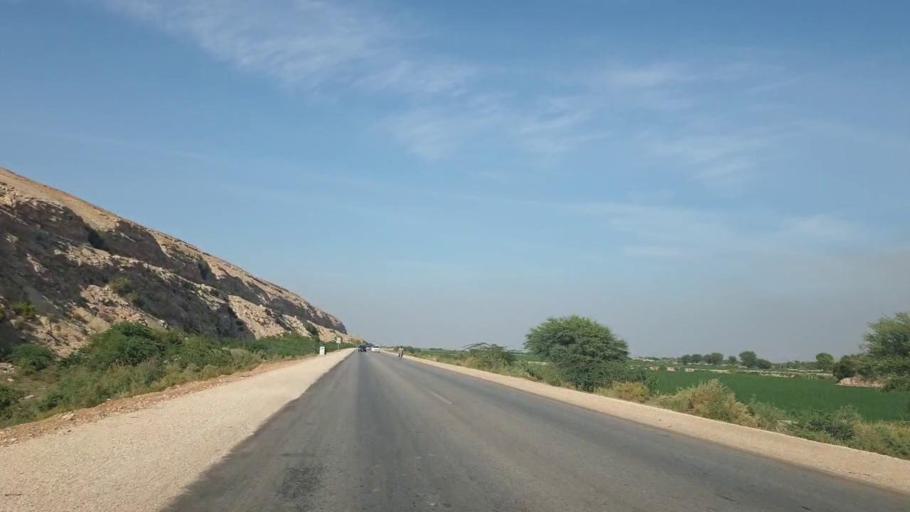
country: PK
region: Sindh
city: Sehwan
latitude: 26.3556
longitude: 67.8730
